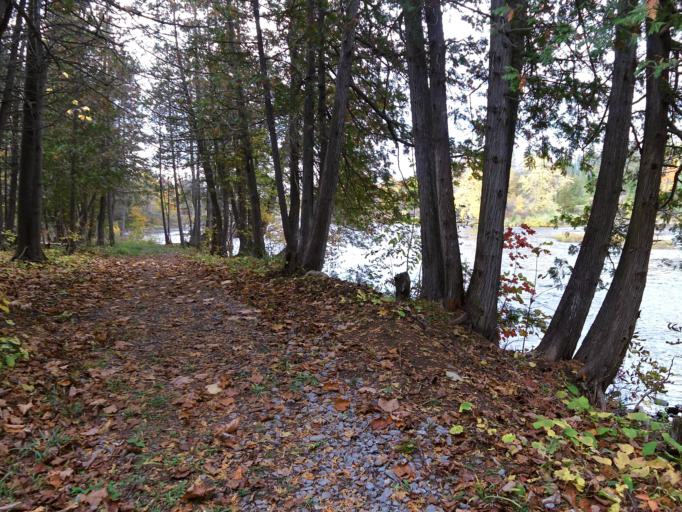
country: CA
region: Ontario
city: Pembroke
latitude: 45.5339
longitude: -77.0908
